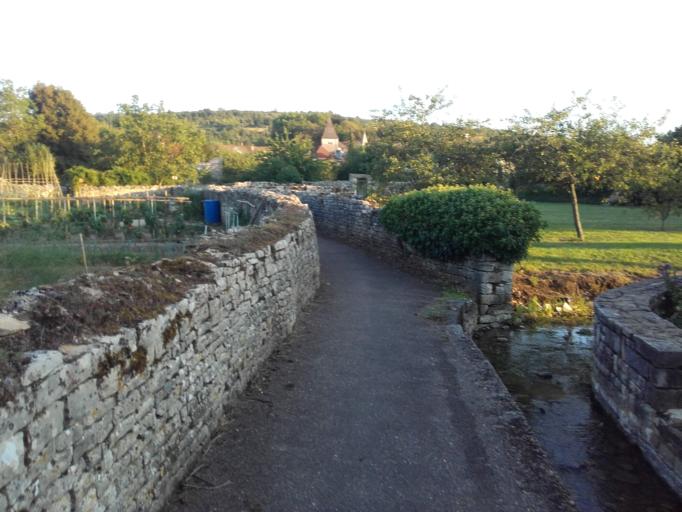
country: FR
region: Bourgogne
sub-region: Departement de Saone-et-Loire
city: Chagny
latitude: 46.9098
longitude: 4.7220
